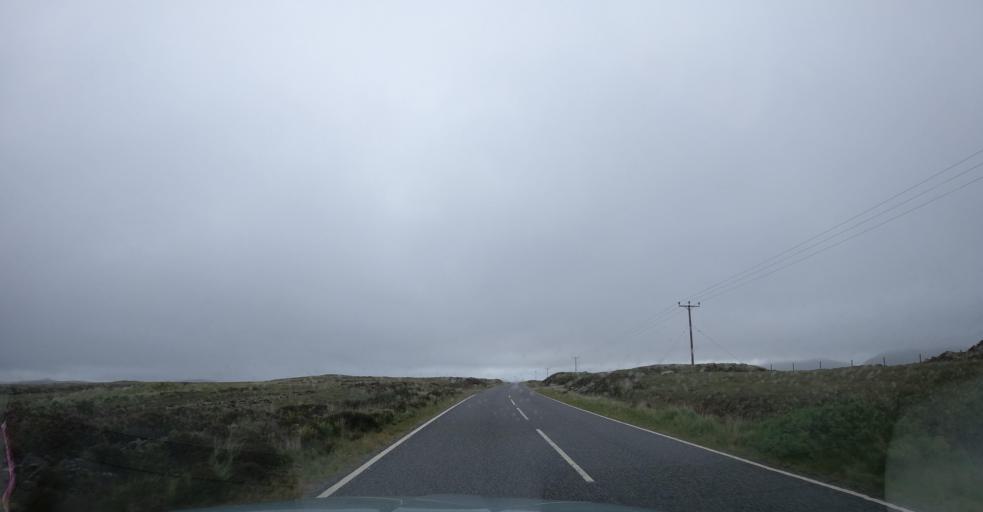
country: GB
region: Scotland
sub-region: Eilean Siar
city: Isle of North Uist
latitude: 57.5868
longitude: -7.2332
